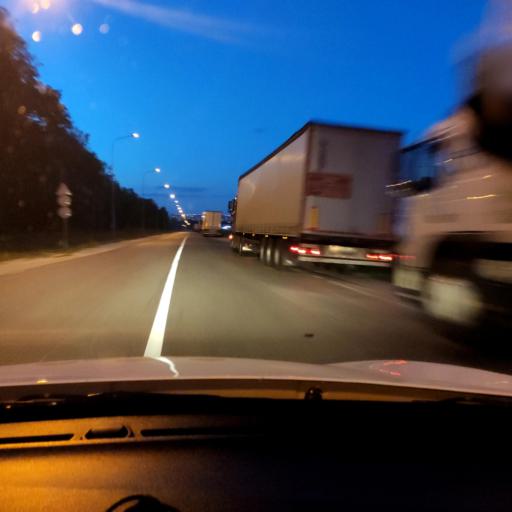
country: RU
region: Tatarstan
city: Osinovo
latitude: 55.8484
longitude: 48.8290
